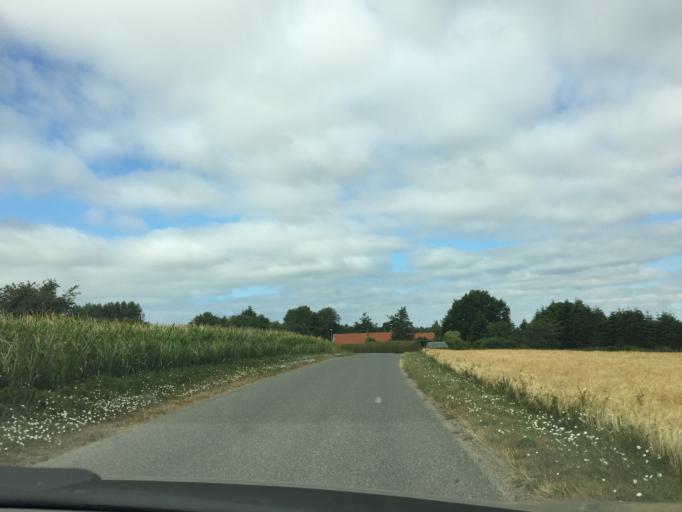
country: DK
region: South Denmark
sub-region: Middelfart Kommune
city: Norre Aby
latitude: 55.5017
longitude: 9.8418
